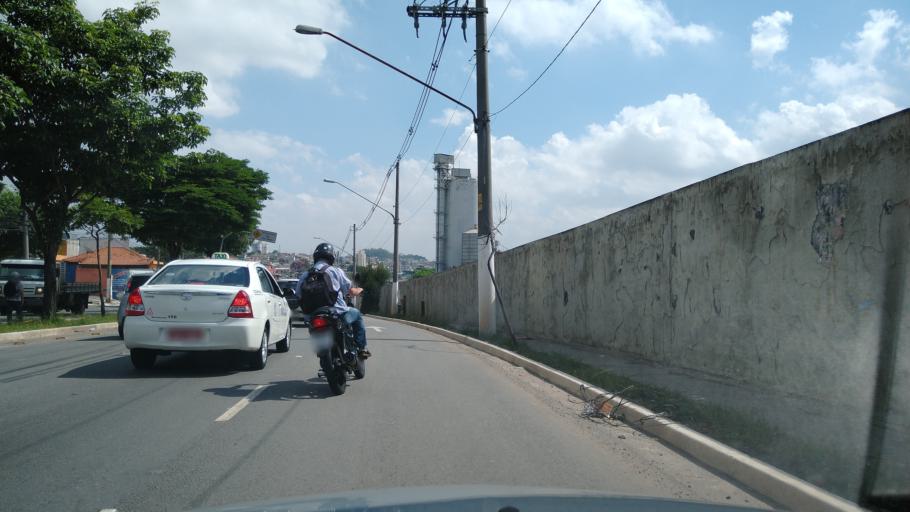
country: BR
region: Sao Paulo
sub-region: Guarulhos
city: Guarulhos
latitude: -23.4828
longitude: -46.4720
